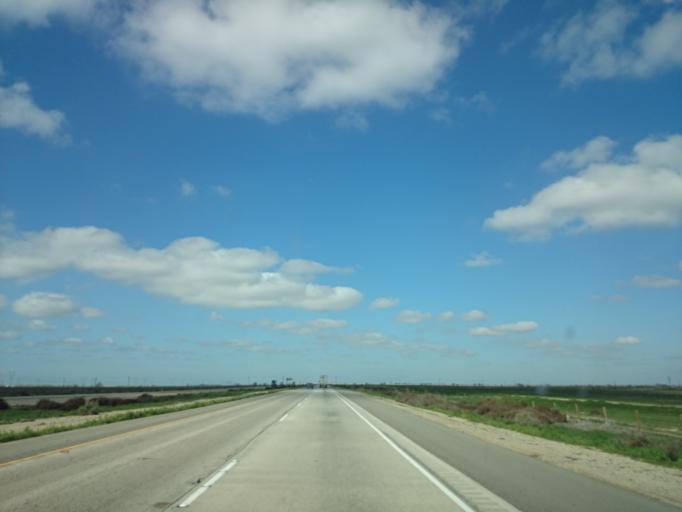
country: US
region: California
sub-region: Kern County
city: Rosedale
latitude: 35.3162
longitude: -119.2811
